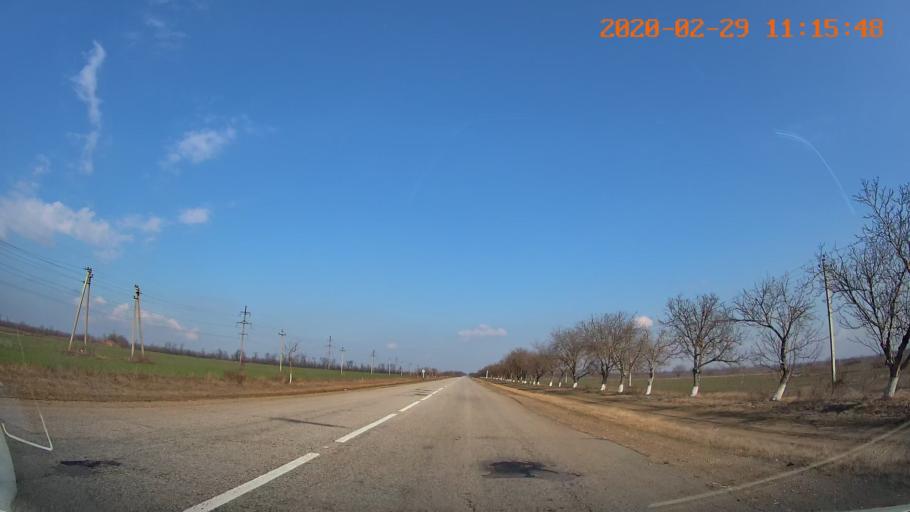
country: MD
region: Telenesti
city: Dubasari
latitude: 47.2997
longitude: 29.1661
